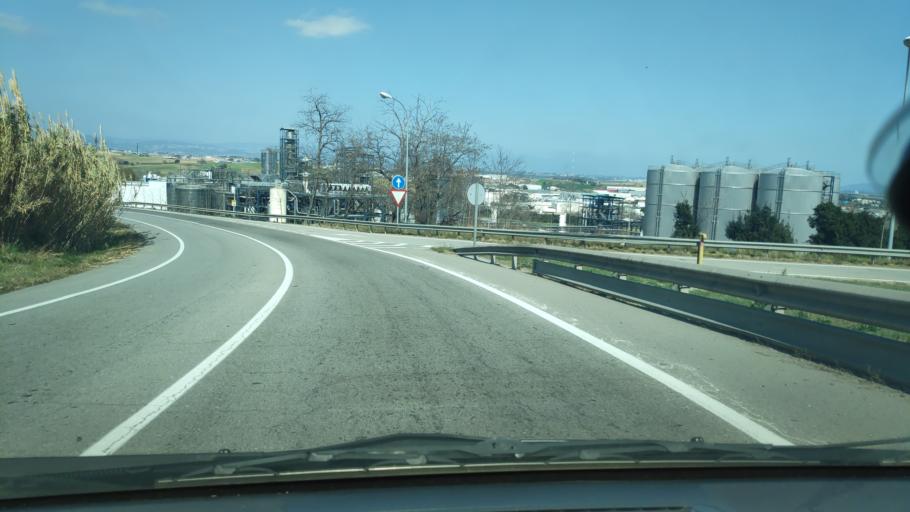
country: ES
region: Catalonia
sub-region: Provincia de Barcelona
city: Polinya
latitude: 41.5271
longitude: 2.1528
